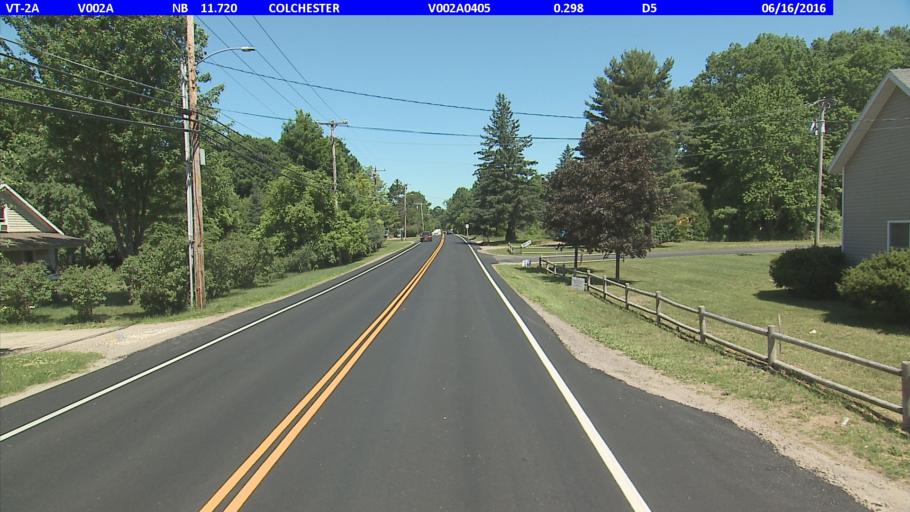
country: US
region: Vermont
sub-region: Chittenden County
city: Colchester
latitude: 44.5318
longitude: -73.1327
